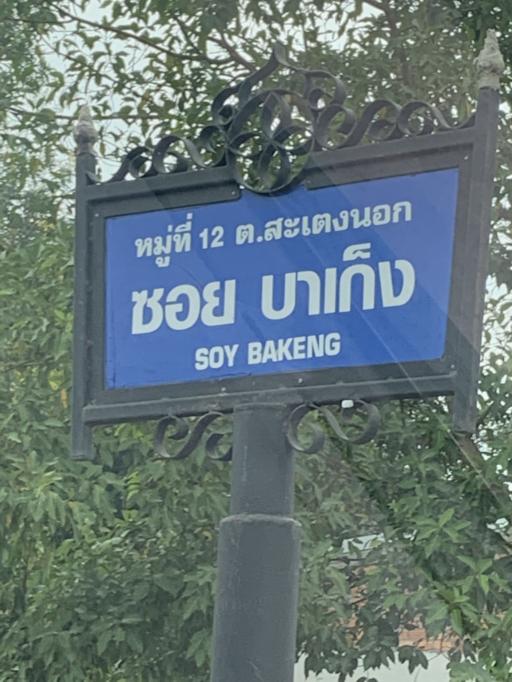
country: TH
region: Yala
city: Yala
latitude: 6.5284
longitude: 101.2912
